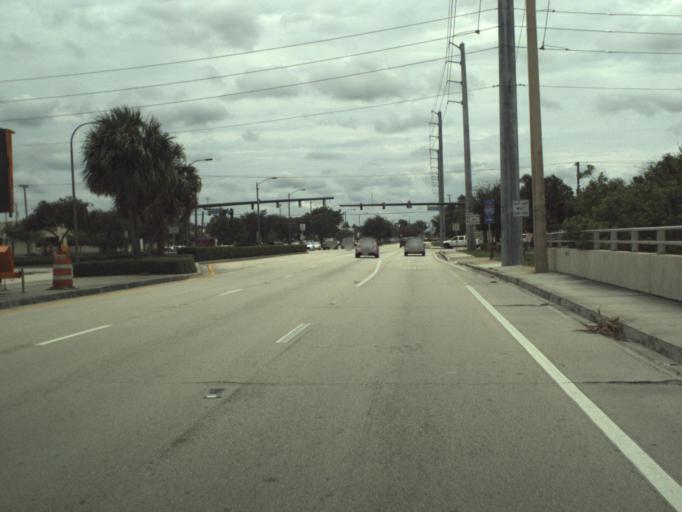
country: US
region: Florida
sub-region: Palm Beach County
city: Lake Park
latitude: 26.8086
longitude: -80.0563
